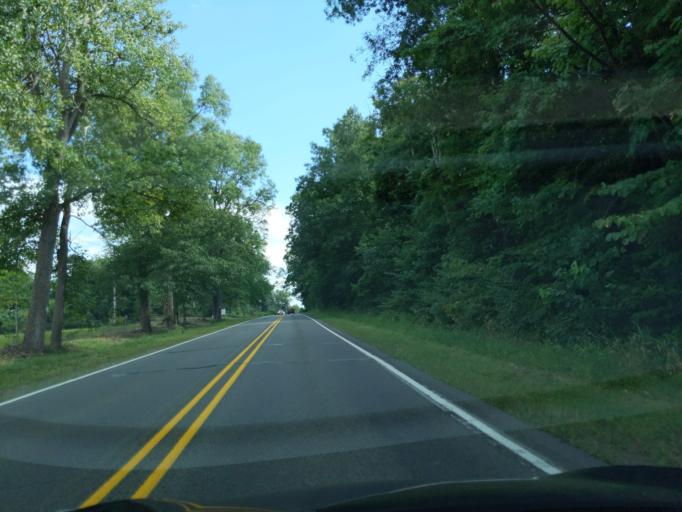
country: US
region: Michigan
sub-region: Jackson County
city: Jackson
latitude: 42.2825
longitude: -84.4578
